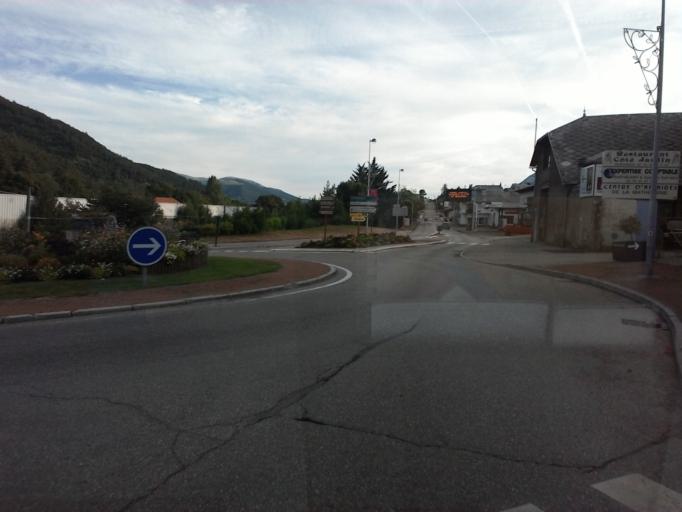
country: FR
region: Rhone-Alpes
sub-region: Departement de l'Isere
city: La Mure
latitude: 44.9099
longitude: 5.7840
